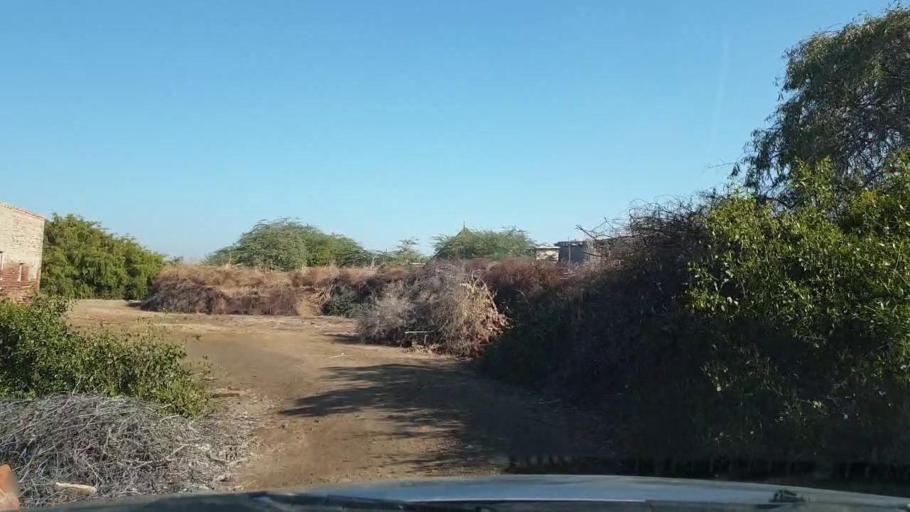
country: PK
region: Sindh
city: Jhol
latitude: 25.8189
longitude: 68.9665
